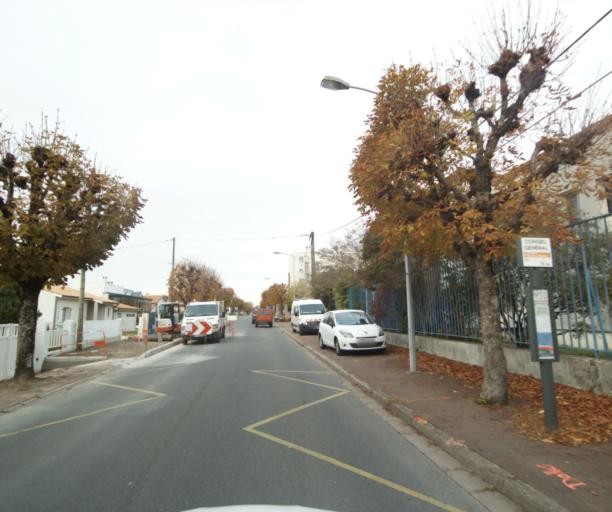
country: FR
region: Poitou-Charentes
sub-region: Departement de la Charente-Maritime
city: Saintes
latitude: 45.7447
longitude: -0.6551
